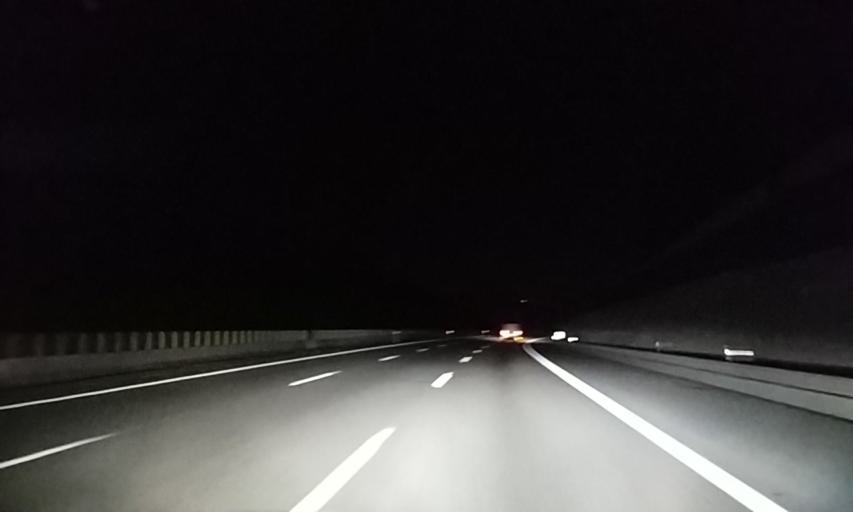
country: PT
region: Aveiro
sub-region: Ovar
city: Sao Joao
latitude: 40.8852
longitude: -8.5646
